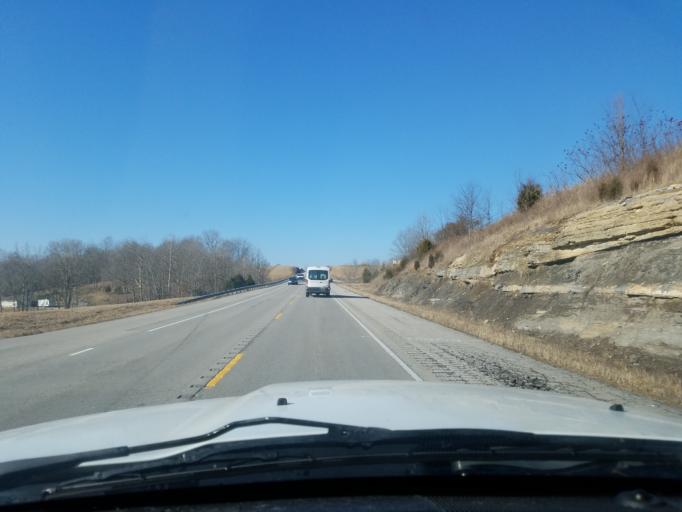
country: US
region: Kentucky
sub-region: Taylor County
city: Campbellsville
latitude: 37.3921
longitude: -85.4518
